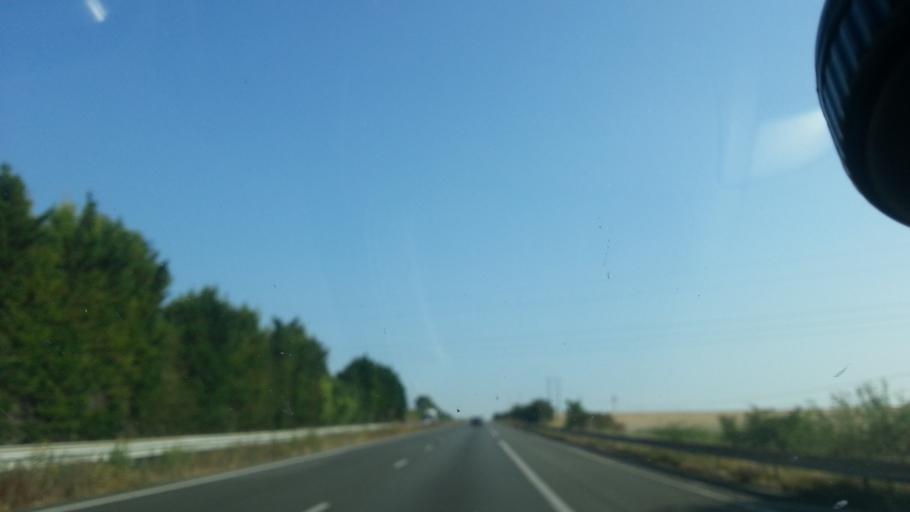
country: FR
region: Poitou-Charentes
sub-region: Departement de la Vienne
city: Antran
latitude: 46.8878
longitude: 0.5184
